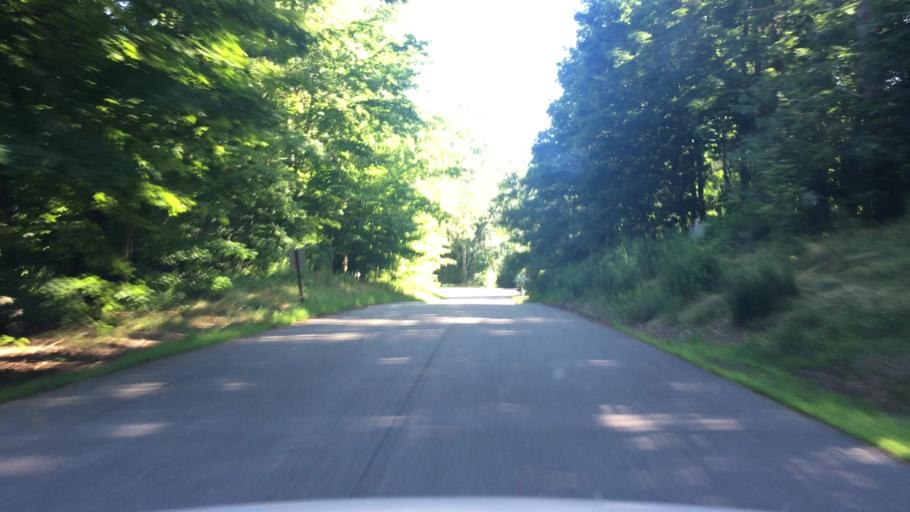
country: US
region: New Hampshire
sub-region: Rockingham County
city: Exeter
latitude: 43.0336
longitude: -70.9638
